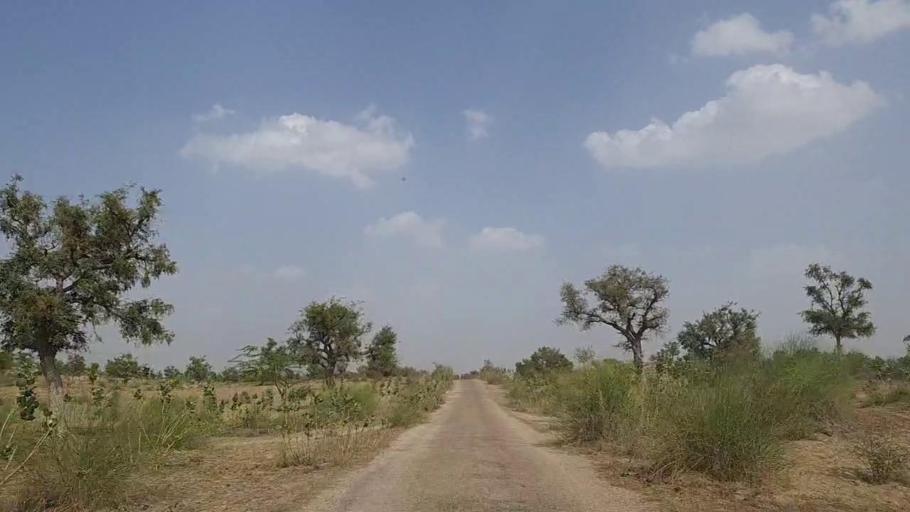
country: PK
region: Sindh
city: Islamkot
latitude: 24.8300
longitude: 70.1500
